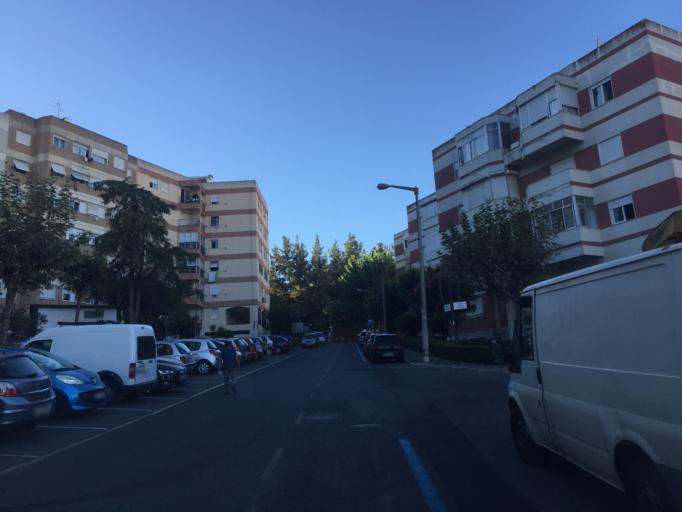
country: PT
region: Lisbon
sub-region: Odivelas
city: Povoa de Santo Adriao
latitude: 38.7992
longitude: -9.1637
